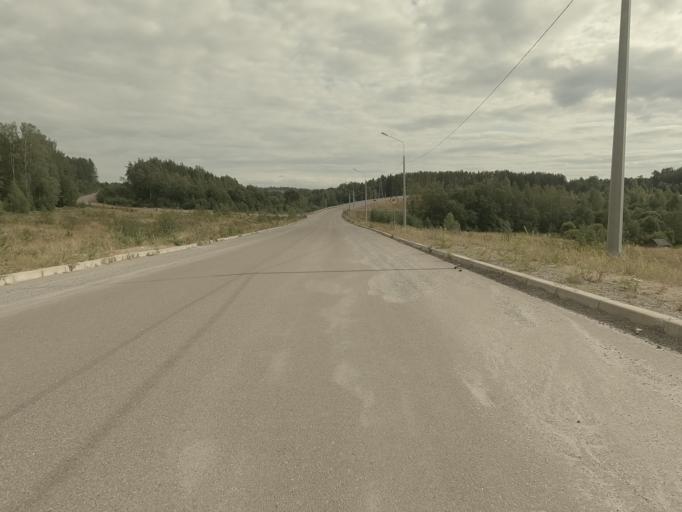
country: RU
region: Leningrad
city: Kamennogorsk
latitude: 60.9667
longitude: 29.1393
